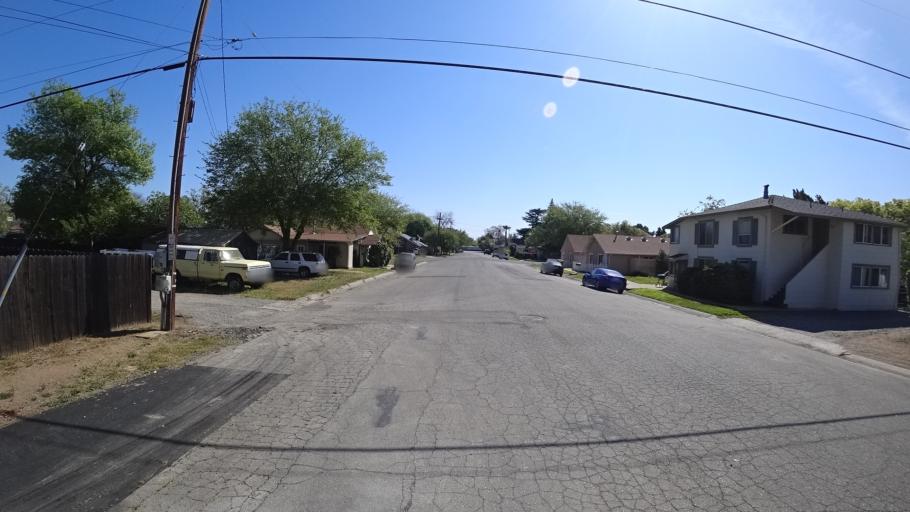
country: US
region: California
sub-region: Glenn County
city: Willows
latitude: 39.5218
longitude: -122.2055
